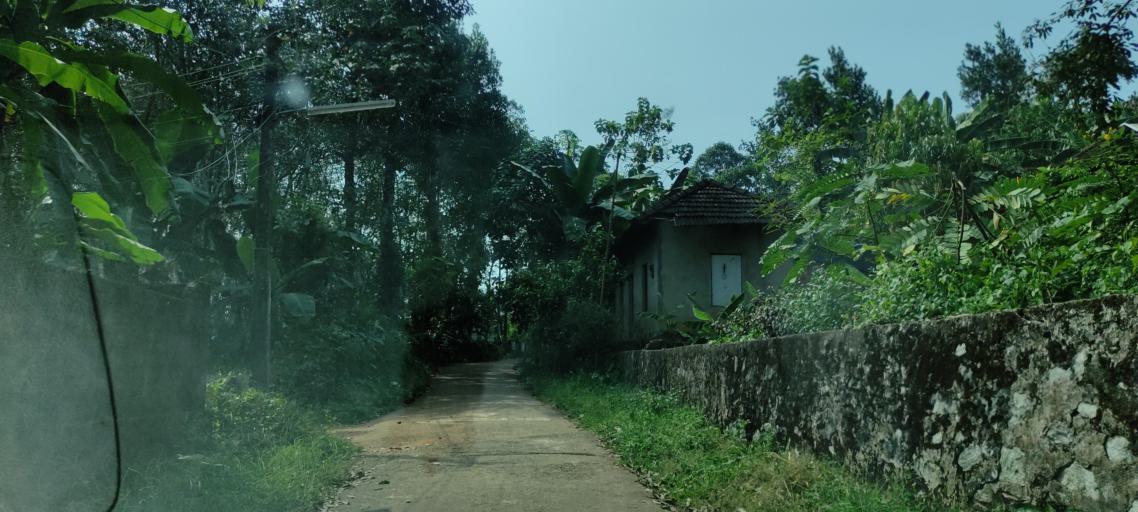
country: IN
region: Kerala
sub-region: Pattanamtitta
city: Adur
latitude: 9.2133
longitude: 76.6940
